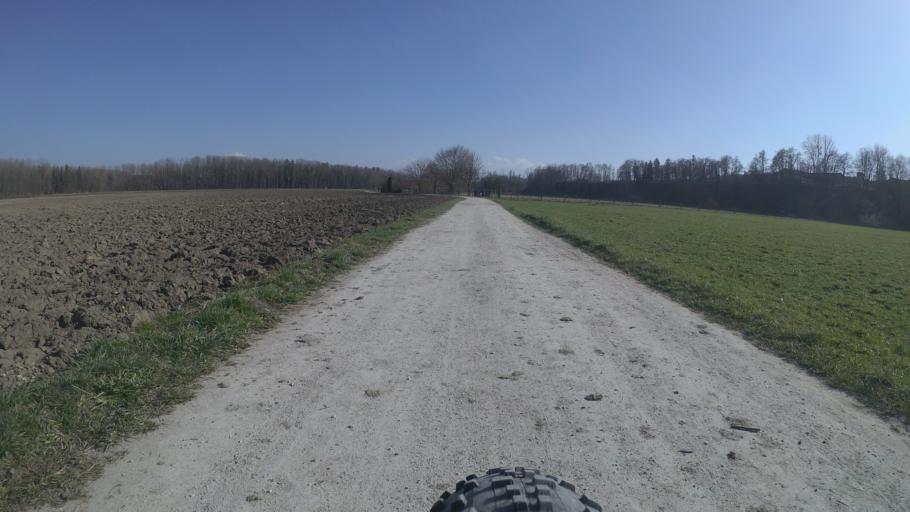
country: DE
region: Bavaria
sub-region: Upper Bavaria
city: Nussdorf
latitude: 47.9314
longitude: 12.6067
